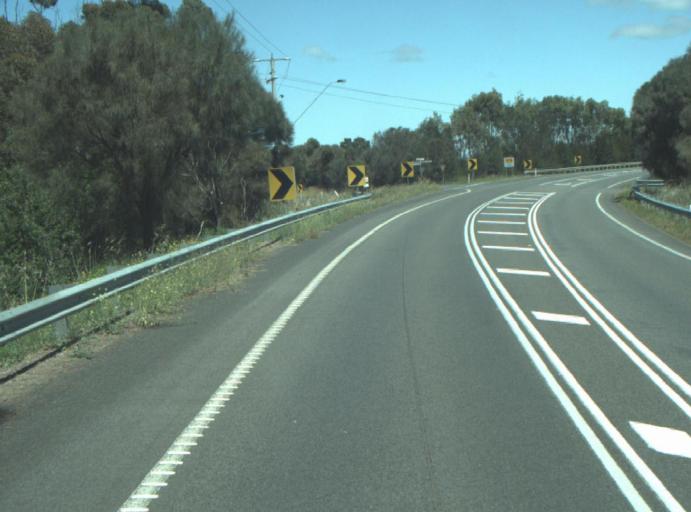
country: AU
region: Victoria
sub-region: Queenscliffe
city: Queenscliff
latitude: -38.1858
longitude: 144.6810
